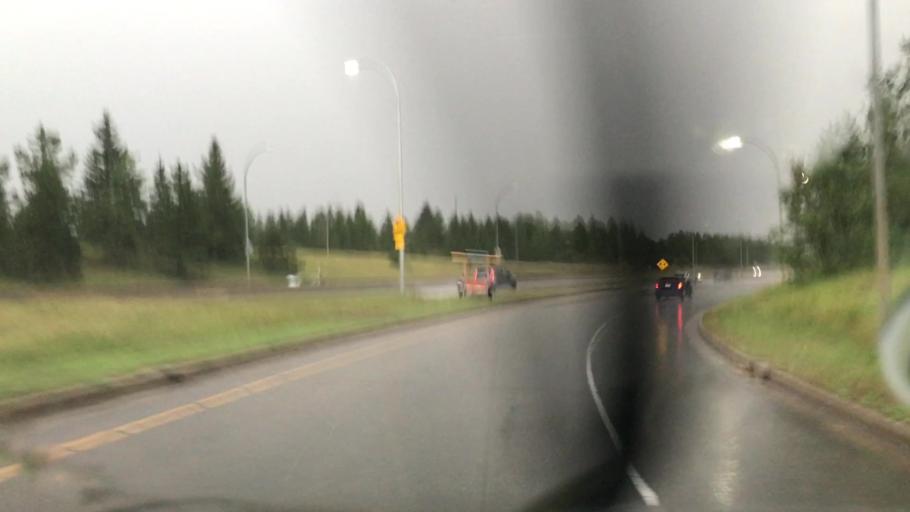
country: CA
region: Alberta
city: Edmonton
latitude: 53.4822
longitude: -113.5690
